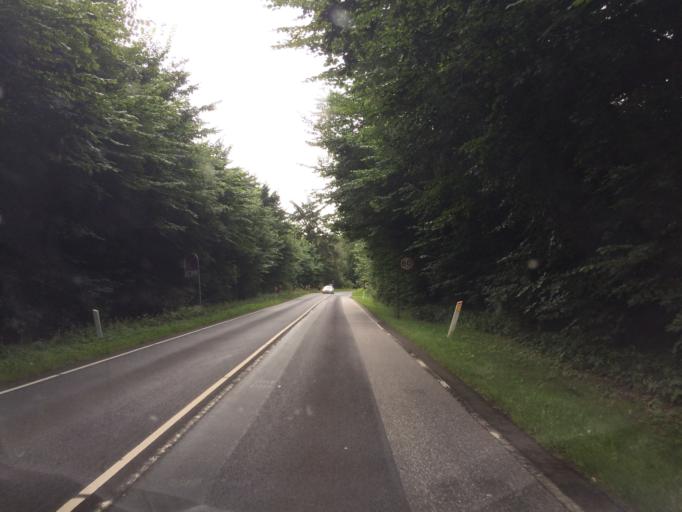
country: DK
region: South Denmark
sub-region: Faaborg-Midtfyn Kommune
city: Faaborg
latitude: 55.1272
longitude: 10.2561
